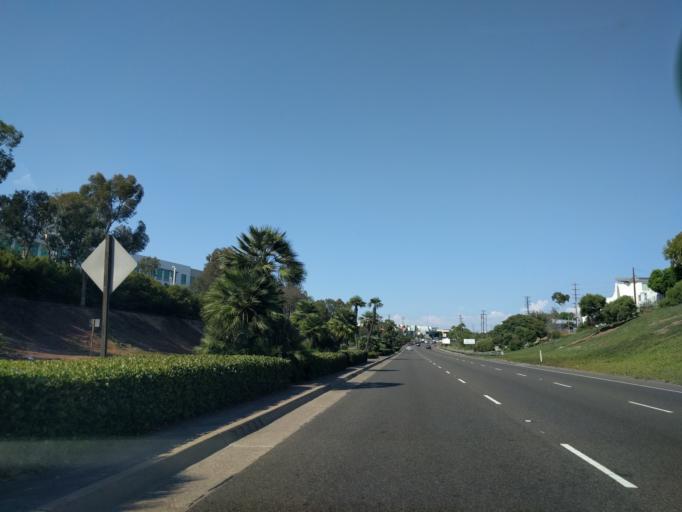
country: US
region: California
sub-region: Orange County
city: Newport Beach
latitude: 33.6275
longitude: -117.9273
